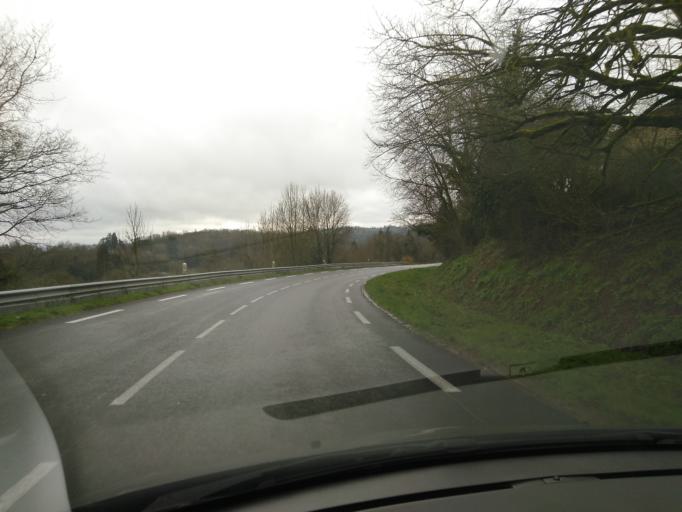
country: FR
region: Limousin
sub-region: Departement de la Haute-Vienne
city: Le Vigen
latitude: 45.7649
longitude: 1.2963
